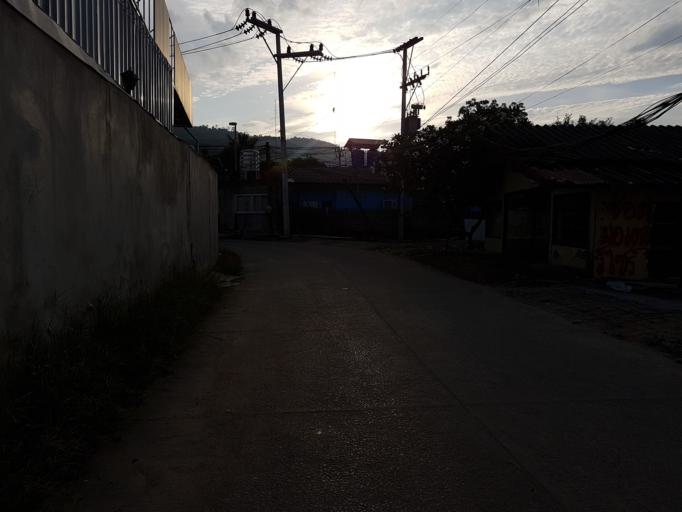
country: TH
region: Surat Thani
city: Ko Samui
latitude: 9.5140
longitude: 100.0513
